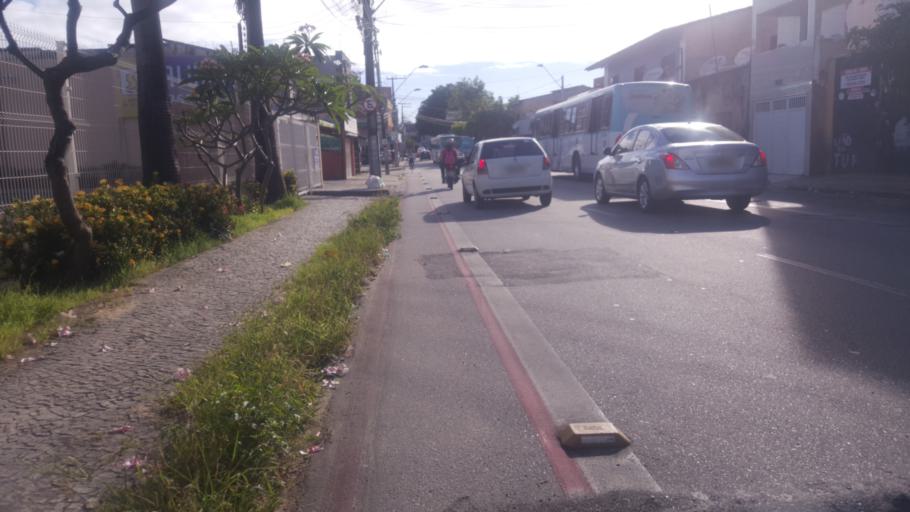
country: BR
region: Ceara
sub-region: Fortaleza
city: Fortaleza
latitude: -3.7558
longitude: -38.5413
